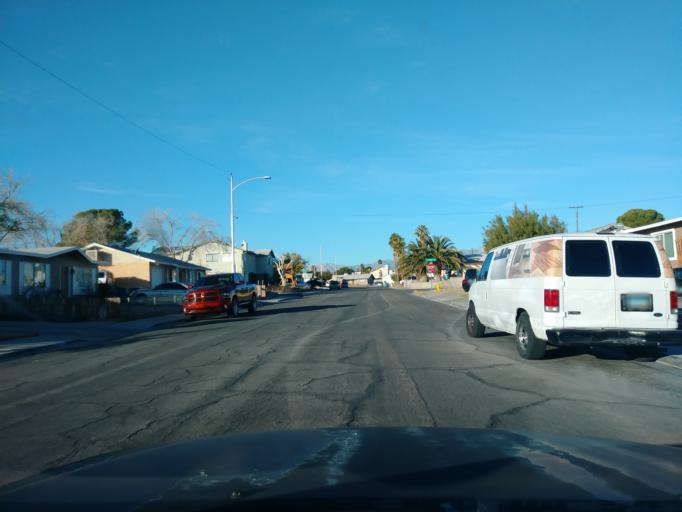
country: US
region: Nevada
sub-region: Clark County
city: Spring Valley
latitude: 36.1644
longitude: -115.2393
